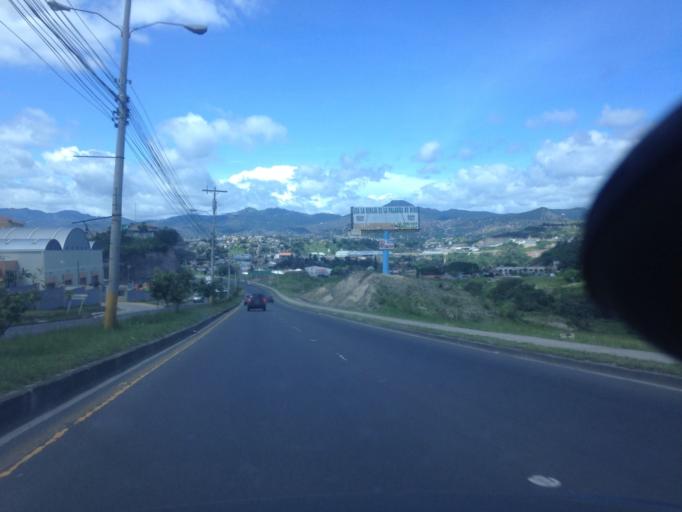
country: HN
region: Francisco Morazan
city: Yaguacire
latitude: 14.0455
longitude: -87.2175
